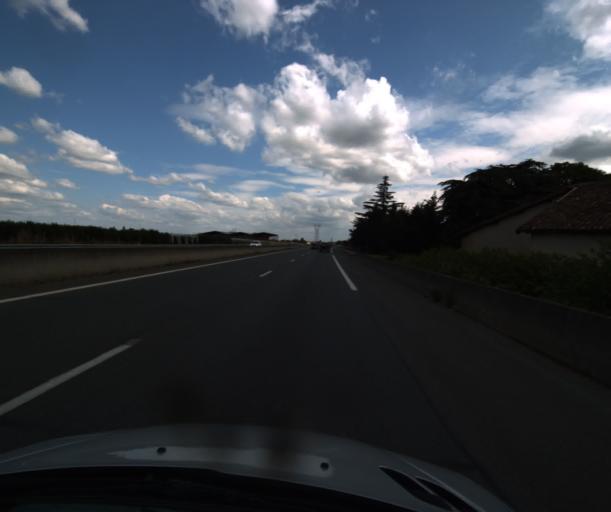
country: FR
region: Midi-Pyrenees
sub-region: Departement du Tarn-et-Garonne
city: Bressols
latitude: 43.9507
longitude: 1.3252
